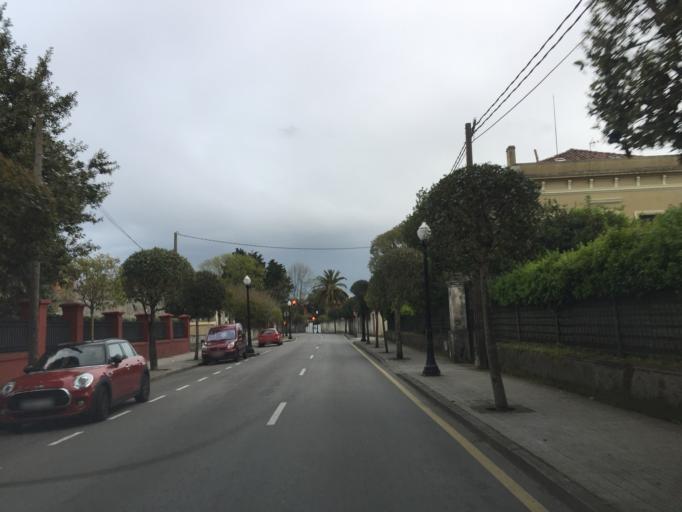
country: ES
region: Asturias
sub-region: Province of Asturias
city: Gijon
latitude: 43.5329
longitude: -5.6301
